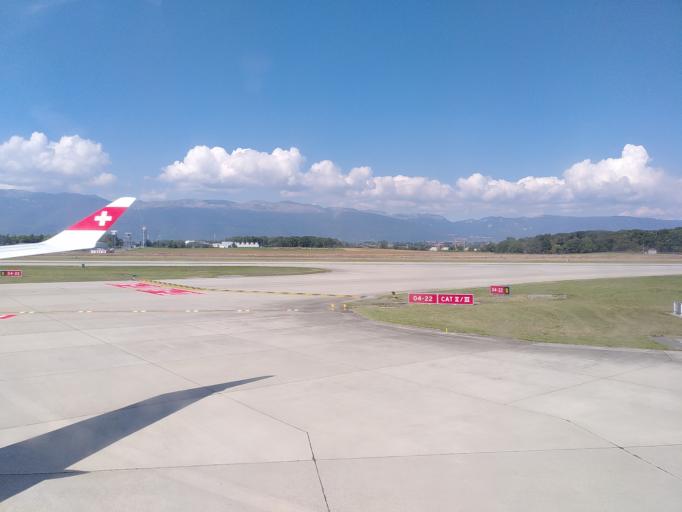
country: CH
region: Geneva
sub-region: Geneva
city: Les Avanchets
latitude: 46.2352
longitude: 6.1078
